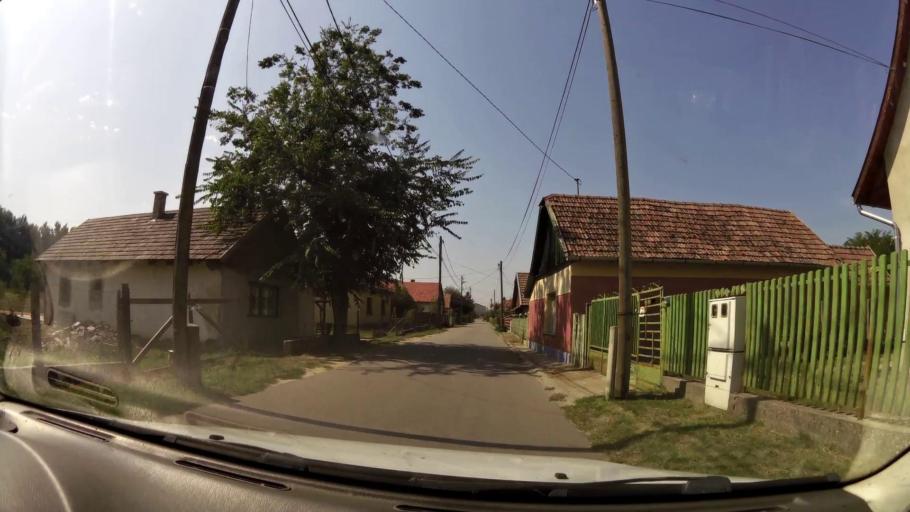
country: HU
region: Pest
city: Ujszilvas
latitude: 47.2708
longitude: 19.9198
